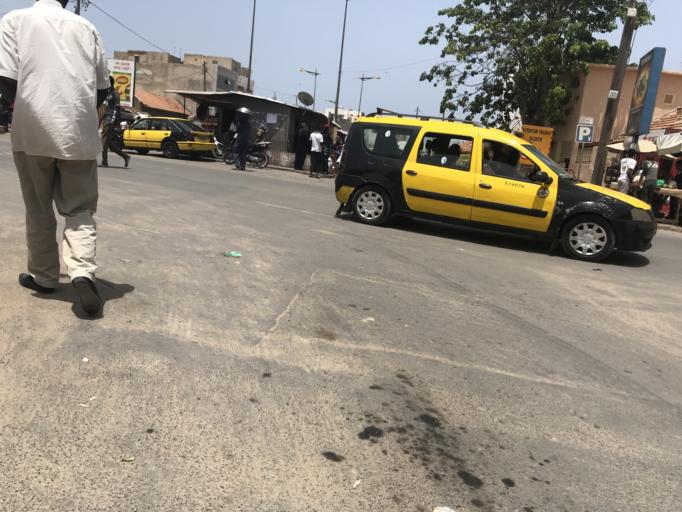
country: SN
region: Dakar
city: Dakar
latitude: 14.6807
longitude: -17.4555
